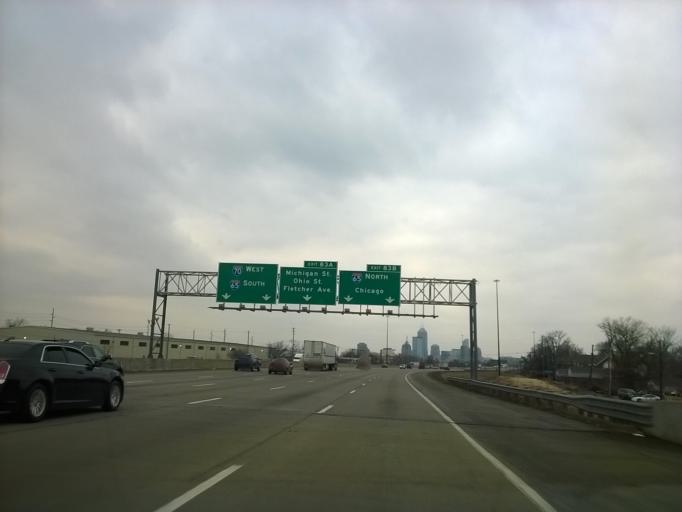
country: US
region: Indiana
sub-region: Marion County
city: Indianapolis
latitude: 39.7913
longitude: -86.1265
